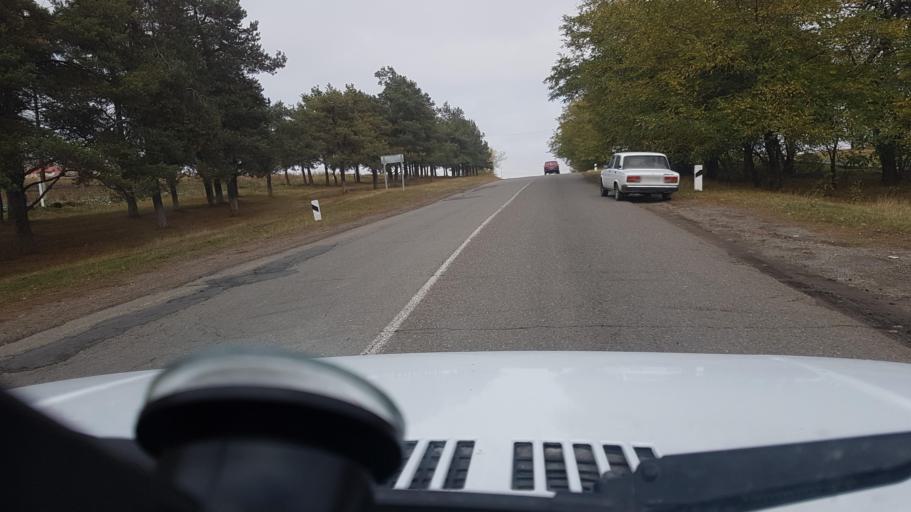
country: AZ
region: Gadabay Rayon
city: Ariqdam
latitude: 40.6373
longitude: 45.8131
